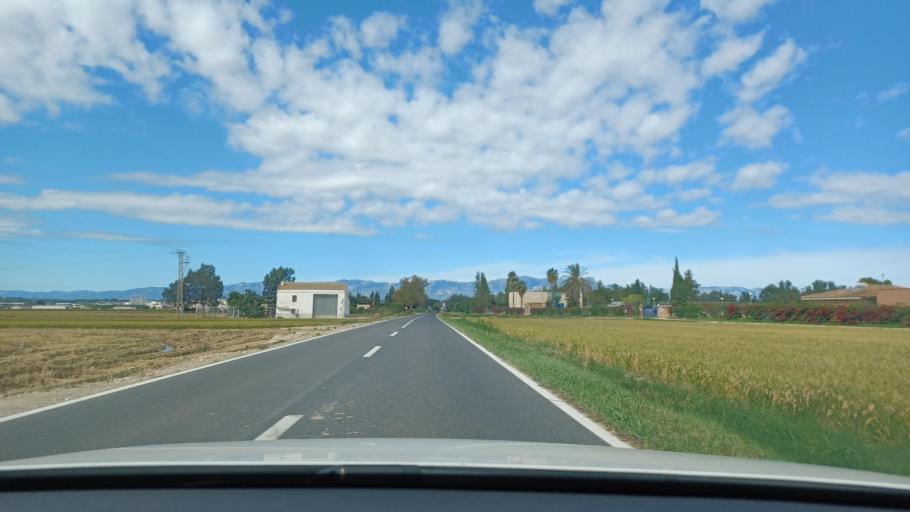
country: ES
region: Catalonia
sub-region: Provincia de Tarragona
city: Amposta
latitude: 40.7031
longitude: 0.6112
